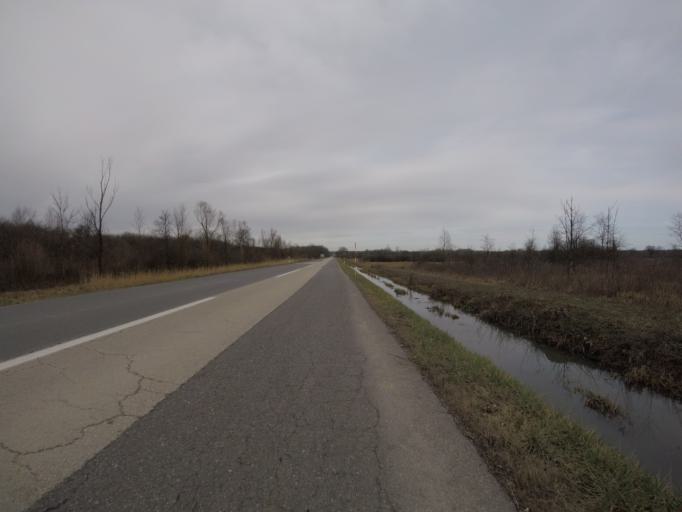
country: HR
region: Grad Zagreb
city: Horvati
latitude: 45.5588
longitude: 15.8606
